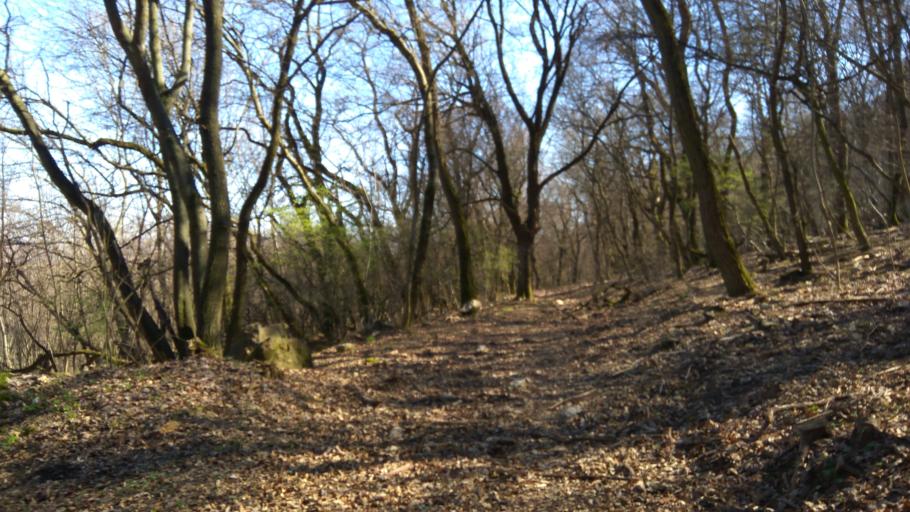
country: HU
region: Pest
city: Pilisborosjeno
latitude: 47.6325
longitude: 18.9886
